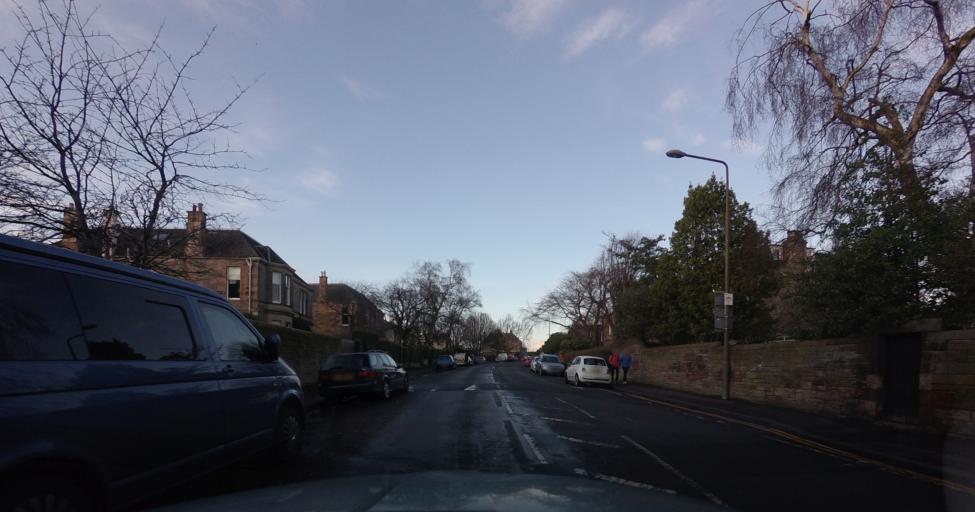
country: GB
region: Scotland
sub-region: Edinburgh
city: Edinburgh
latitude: 55.9668
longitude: -3.2146
